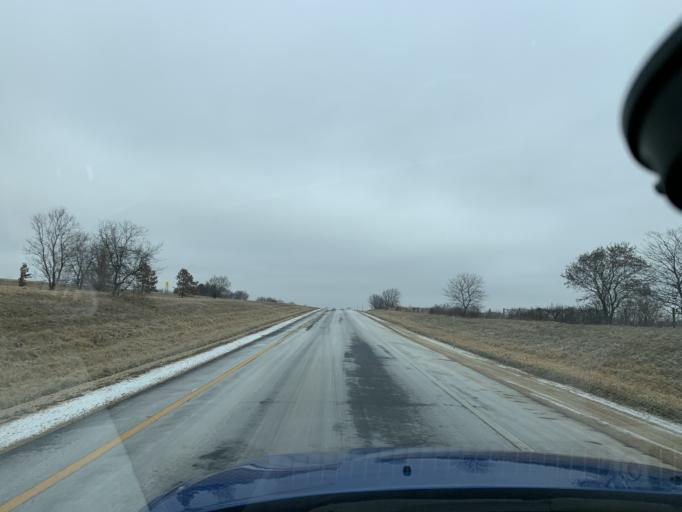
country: US
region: Wisconsin
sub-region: Dane County
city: Sun Prairie
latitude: 43.2398
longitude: -89.1456
